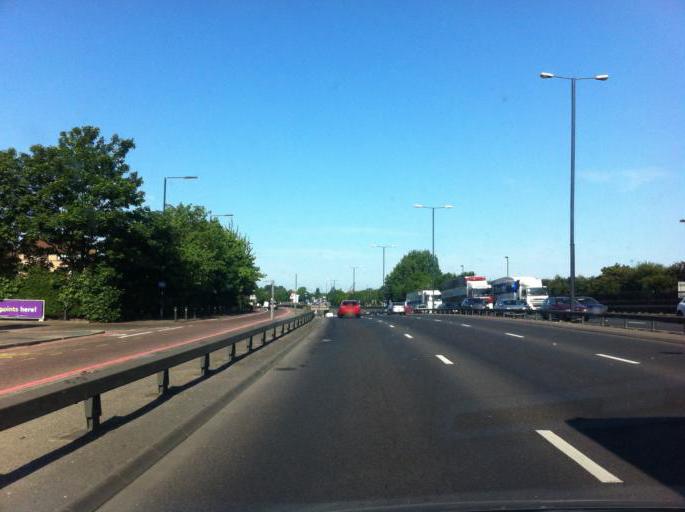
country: GB
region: England
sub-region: Greater London
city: Ealing Broadway
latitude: 51.5335
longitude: -0.3250
